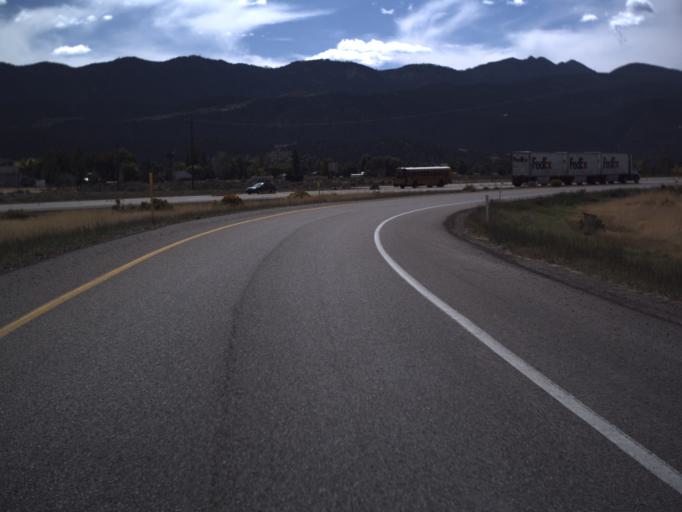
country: US
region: Utah
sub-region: Iron County
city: Parowan
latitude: 37.8584
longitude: -112.8302
